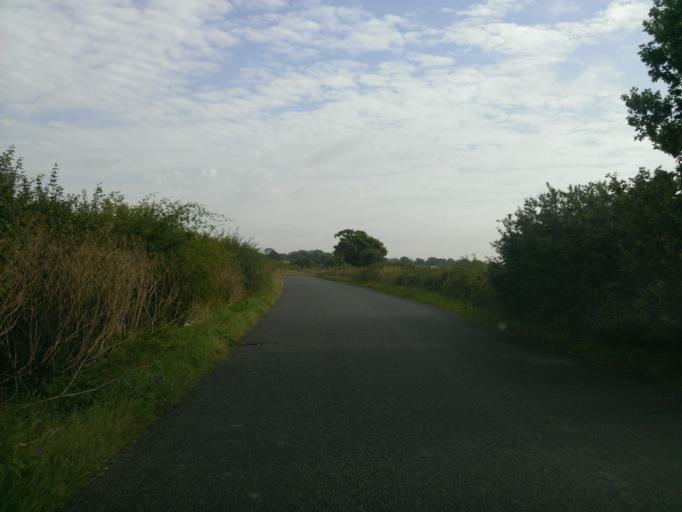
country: GB
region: England
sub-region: Essex
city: Saint Osyth
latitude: 51.8088
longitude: 1.0890
